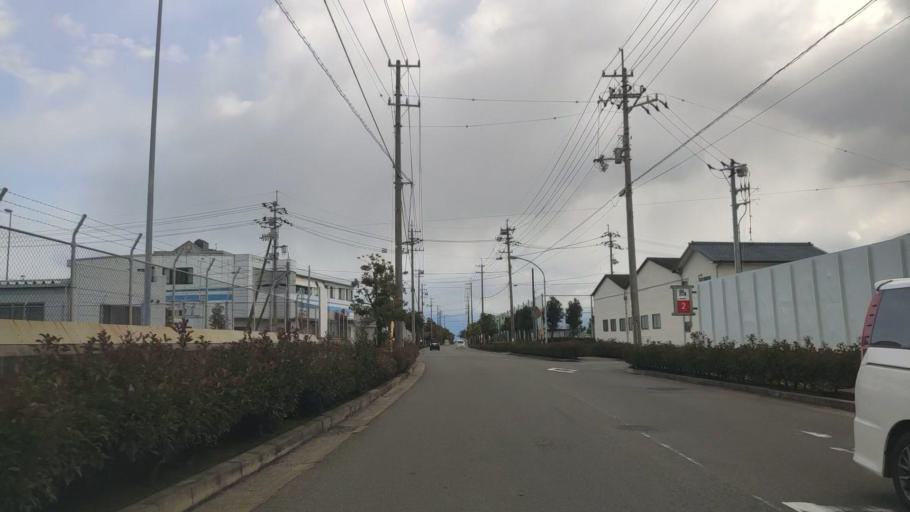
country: JP
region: Ehime
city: Saijo
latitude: 34.0497
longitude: 133.0253
